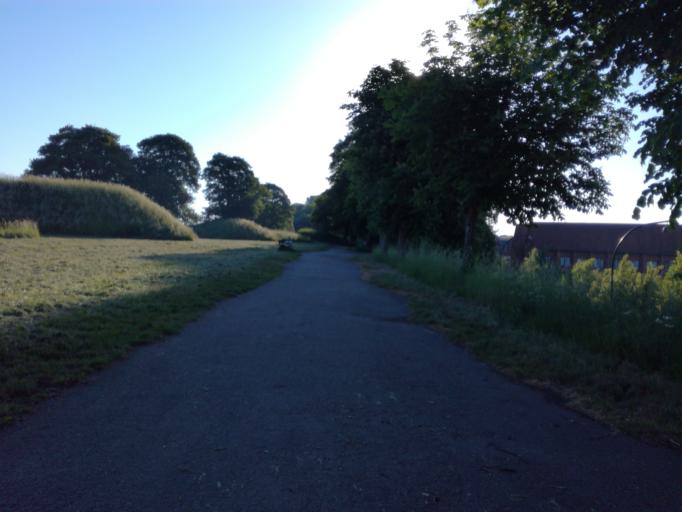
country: DK
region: South Denmark
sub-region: Fredericia Kommune
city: Fredericia
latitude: 55.5693
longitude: 9.7574
